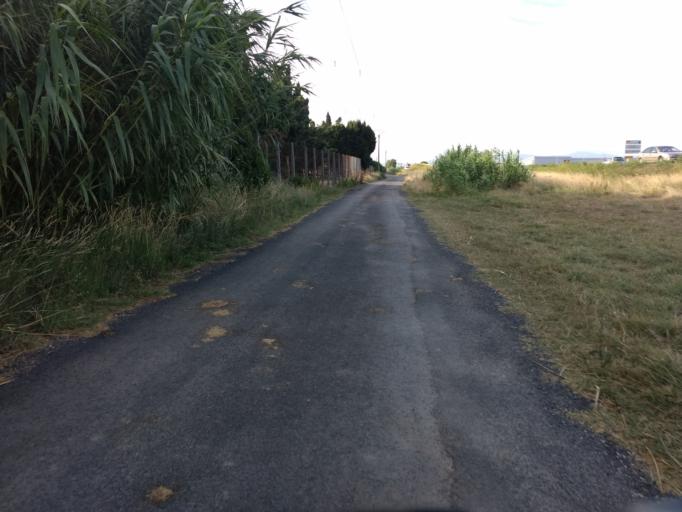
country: FR
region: Languedoc-Roussillon
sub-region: Departement des Pyrenees-Orientales
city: Le Barcares
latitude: 42.7776
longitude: 3.0162
